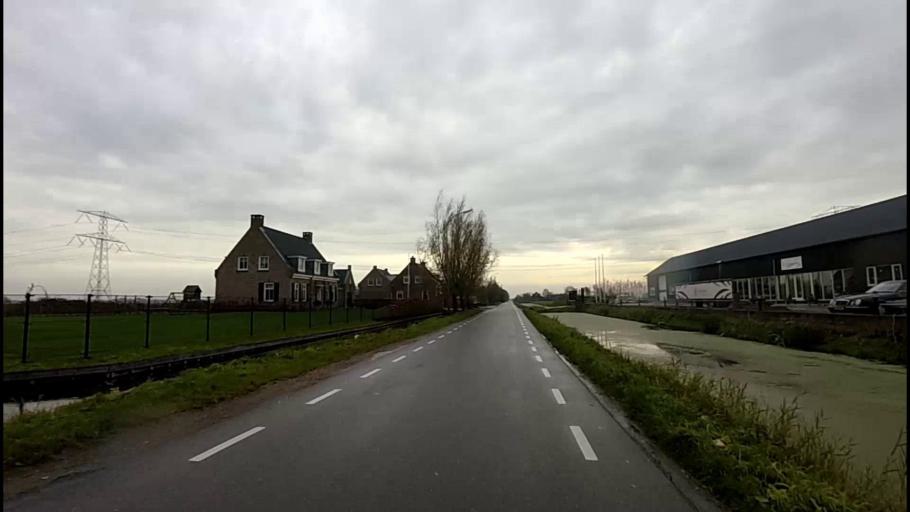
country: NL
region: South Holland
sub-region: Gemeente Krimpen aan den IJssel
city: Krimpen aan den IJssel
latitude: 51.9273
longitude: 4.6455
